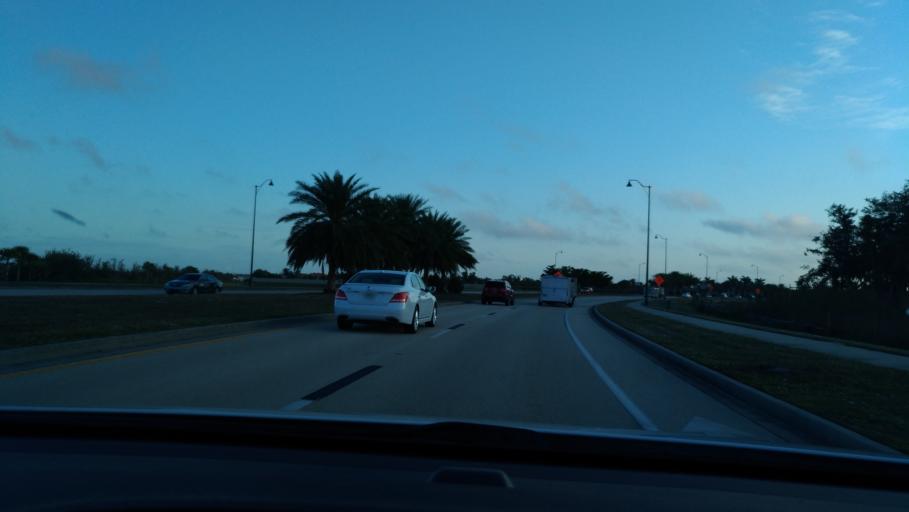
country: US
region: Florida
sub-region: Lee County
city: Bonita Springs
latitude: 26.3653
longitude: -81.7670
